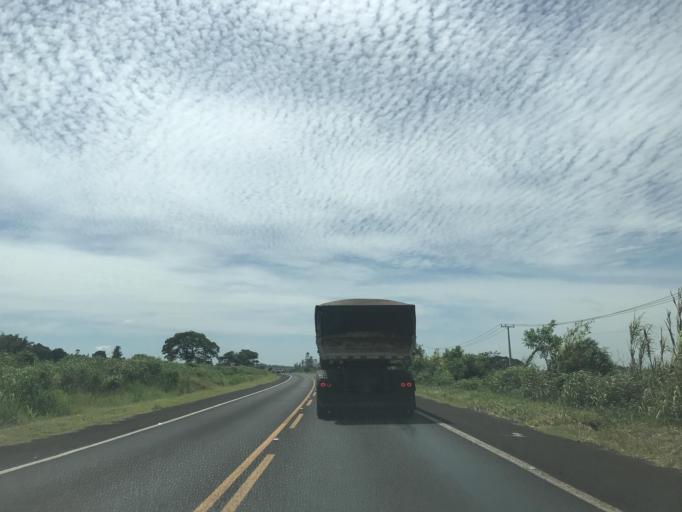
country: BR
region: Parana
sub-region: Paranavai
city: Paranavai
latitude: -23.0154
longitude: -52.5279
